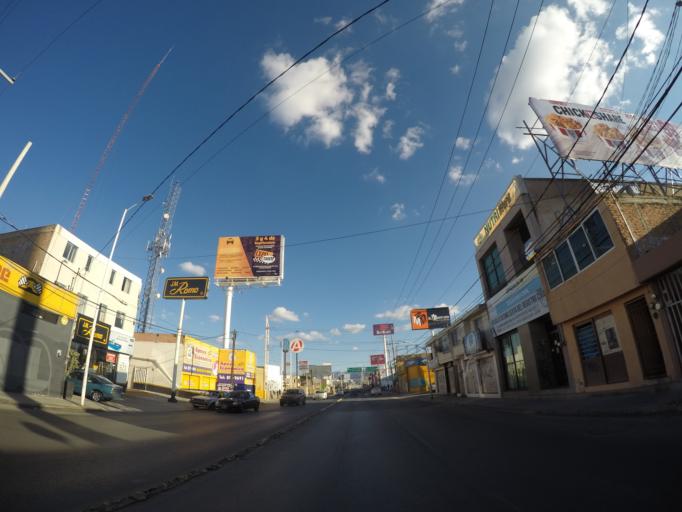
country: MX
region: San Luis Potosi
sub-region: San Luis Potosi
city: San Luis Potosi
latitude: 22.1676
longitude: -101.0016
